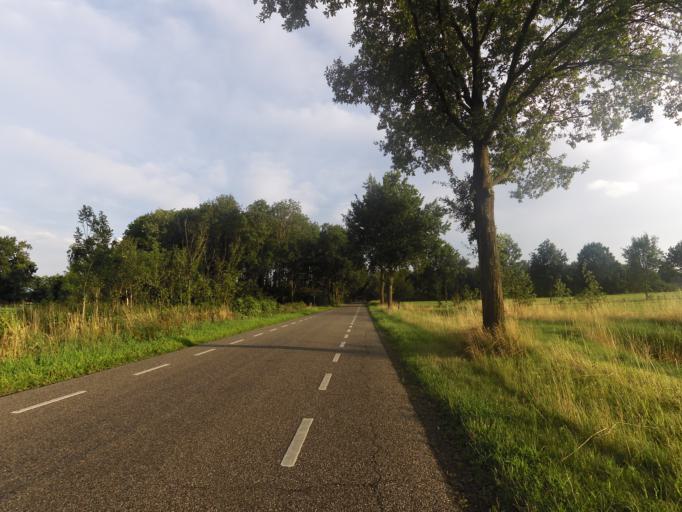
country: NL
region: Gelderland
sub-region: Oude IJsselstreek
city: Varsseveld
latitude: 51.8974
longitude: 6.4870
